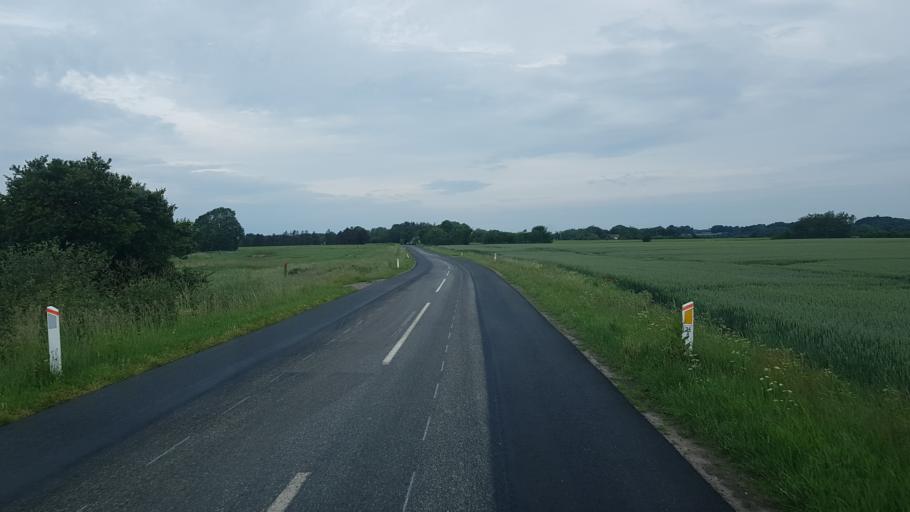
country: DK
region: South Denmark
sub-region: Vejen Kommune
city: Brorup
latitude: 55.4411
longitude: 8.9908
